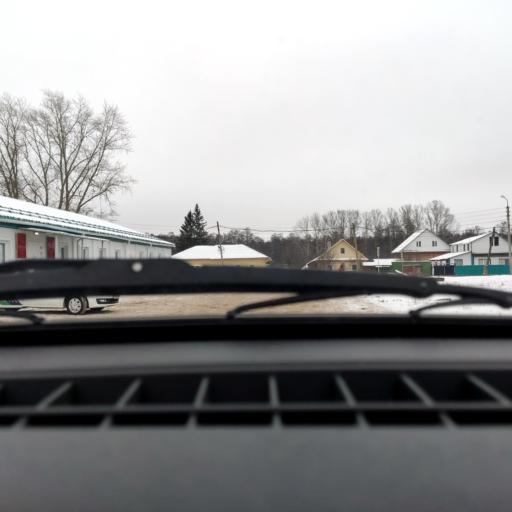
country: RU
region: Bashkortostan
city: Ufa
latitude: 54.8217
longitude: 56.1737
